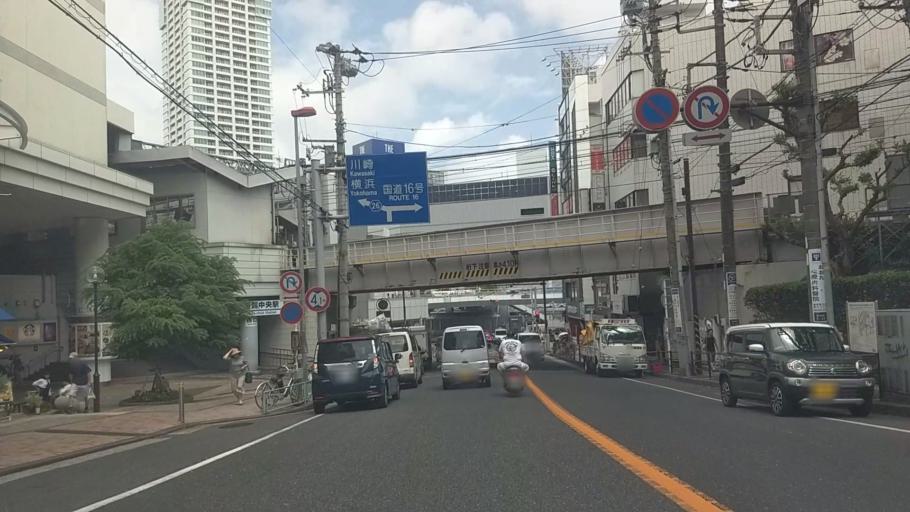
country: JP
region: Kanagawa
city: Yokosuka
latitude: 35.2777
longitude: 139.6708
